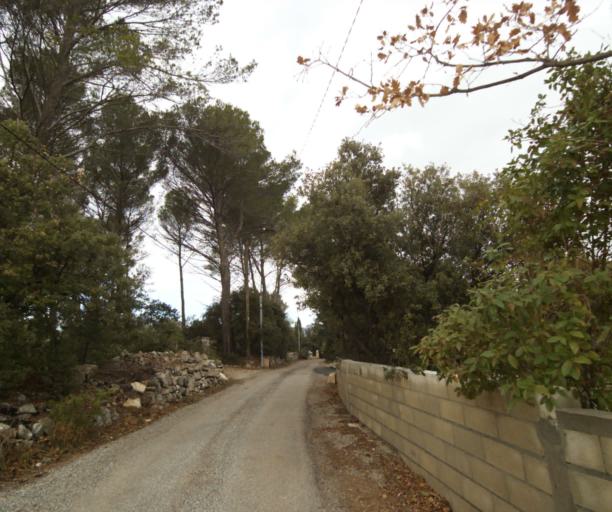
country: FR
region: Provence-Alpes-Cote d'Azur
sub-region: Departement du Var
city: Trans-en-Provence
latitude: 43.5114
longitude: 6.4906
